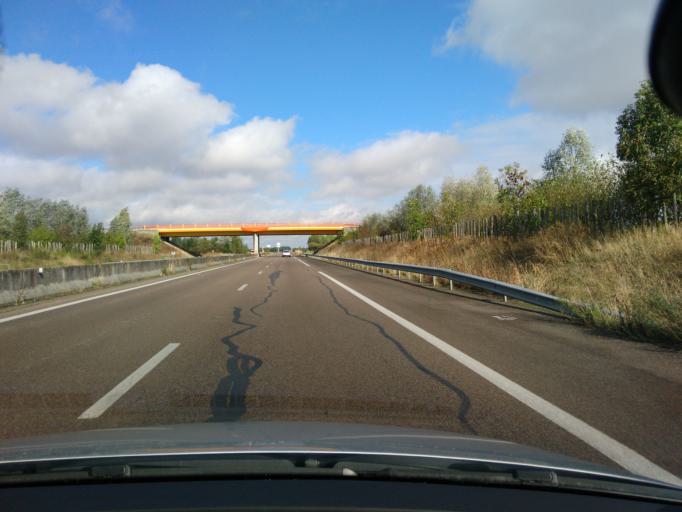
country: FR
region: Haute-Normandie
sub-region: Departement de l'Eure
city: Damville
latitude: 48.8863
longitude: 1.1732
